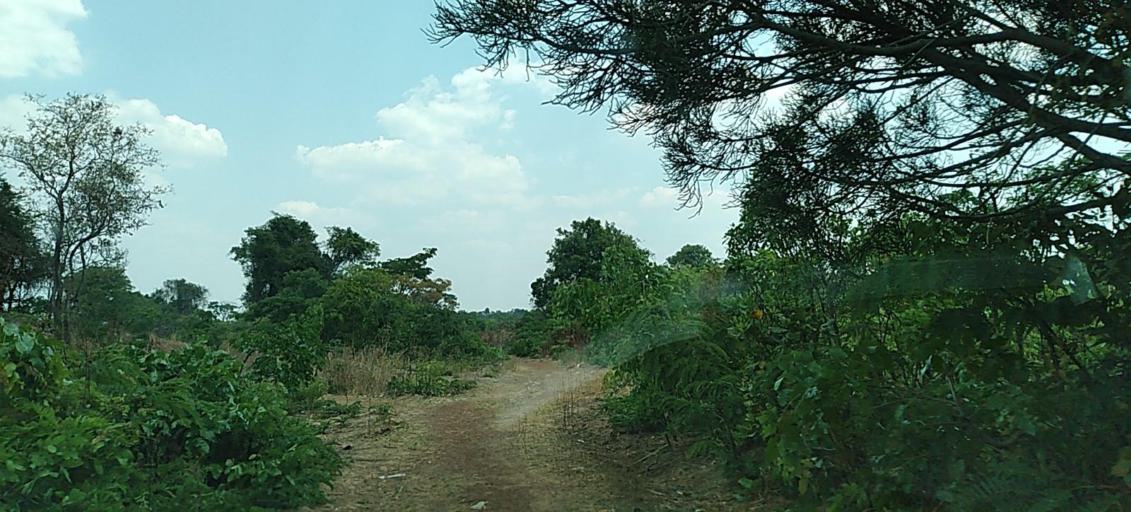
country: CD
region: Katanga
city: Kipushi
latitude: -11.9883
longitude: 27.4161
